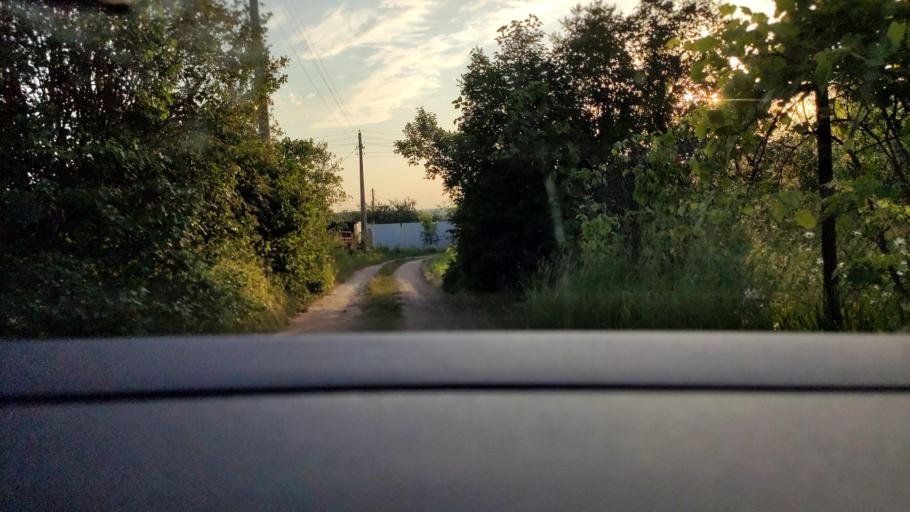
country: RU
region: Voronezj
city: Ramon'
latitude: 51.9119
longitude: 39.1760
